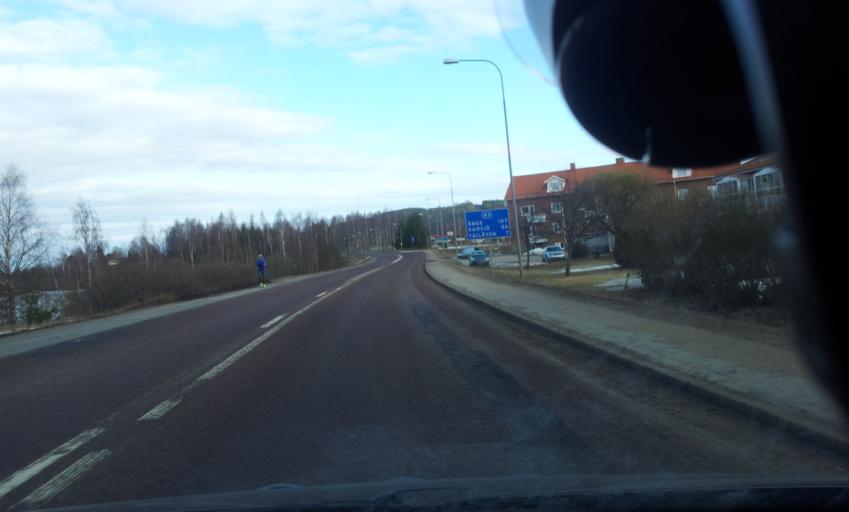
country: SE
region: Gaevleborg
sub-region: Ljusdals Kommun
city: Ljusdal
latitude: 61.8314
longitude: 16.0697
